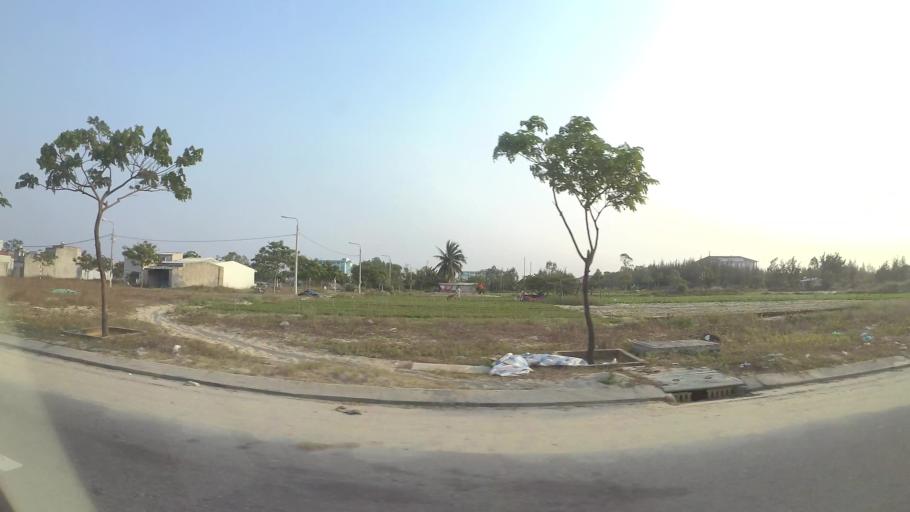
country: VN
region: Da Nang
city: Ngu Hanh Son
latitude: 15.9832
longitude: 108.2471
